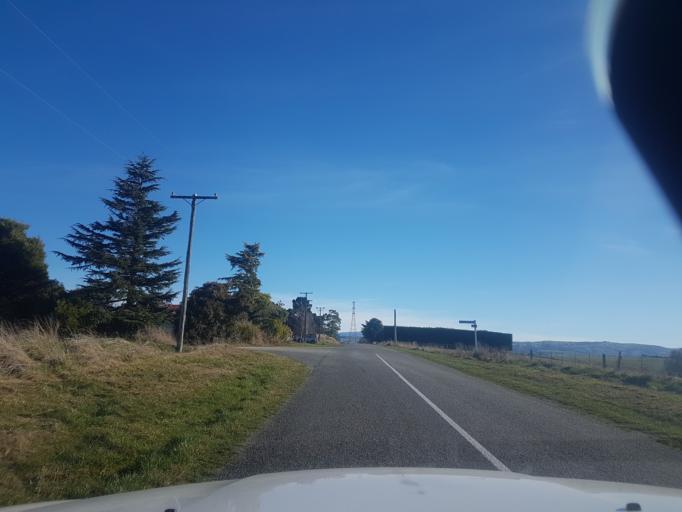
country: NZ
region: Canterbury
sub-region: Timaru District
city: Pleasant Point
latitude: -44.2533
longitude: 171.0438
